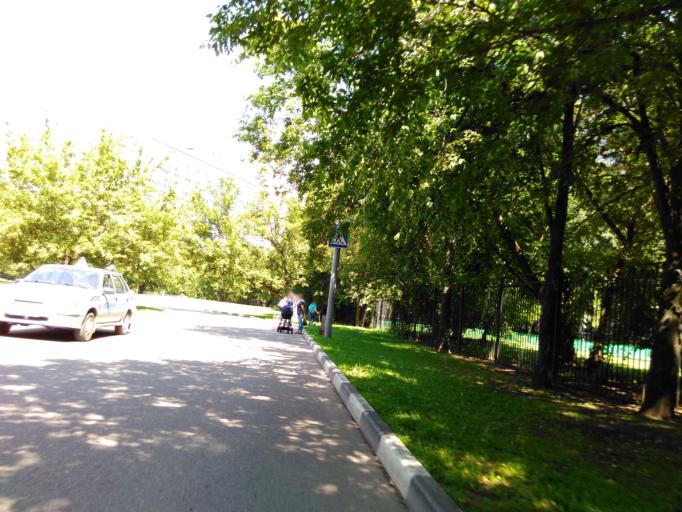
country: RU
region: Moskovskaya
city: Leninskiye Gory
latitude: 55.7032
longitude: 37.5627
